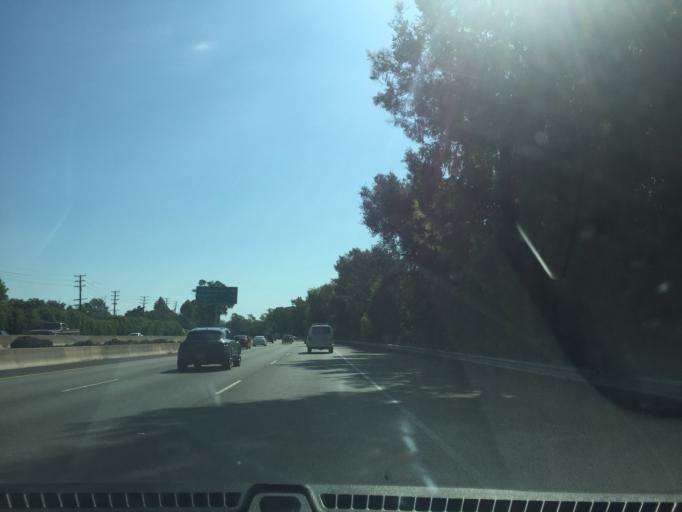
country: US
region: California
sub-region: Santa Barbara County
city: Mission Canyon
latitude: 34.4308
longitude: -119.7439
